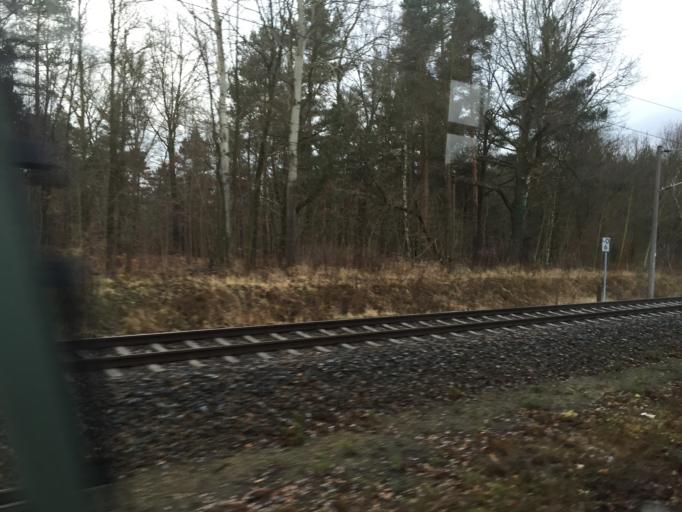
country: DE
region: Saxony
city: Albertstadt
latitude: 51.1156
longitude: 13.7899
